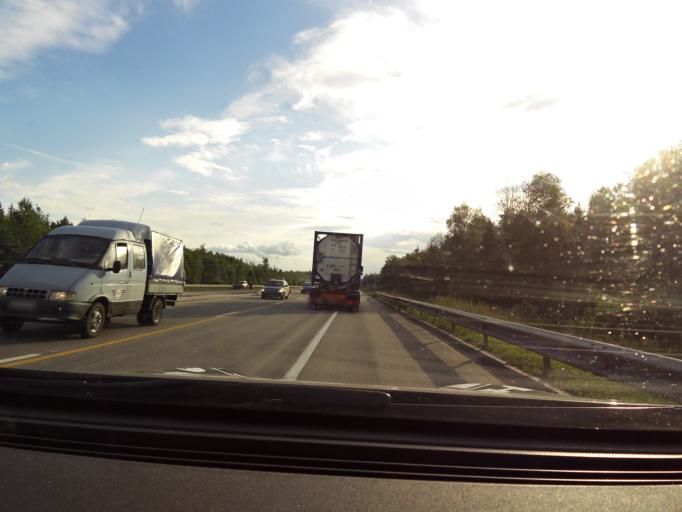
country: RU
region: Vladimir
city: Sudogda
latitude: 56.1090
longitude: 40.8135
